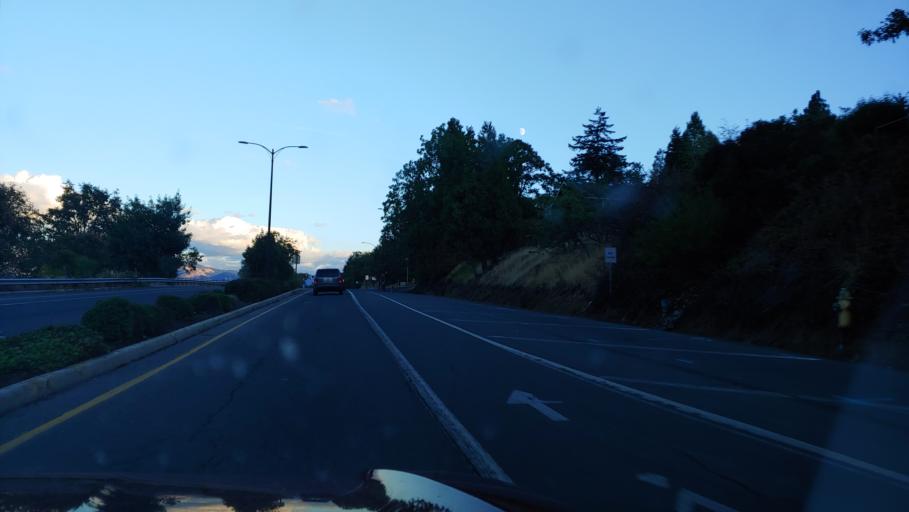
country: US
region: Oregon
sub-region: Jackson County
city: Ashland
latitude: 42.2121
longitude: -122.7289
